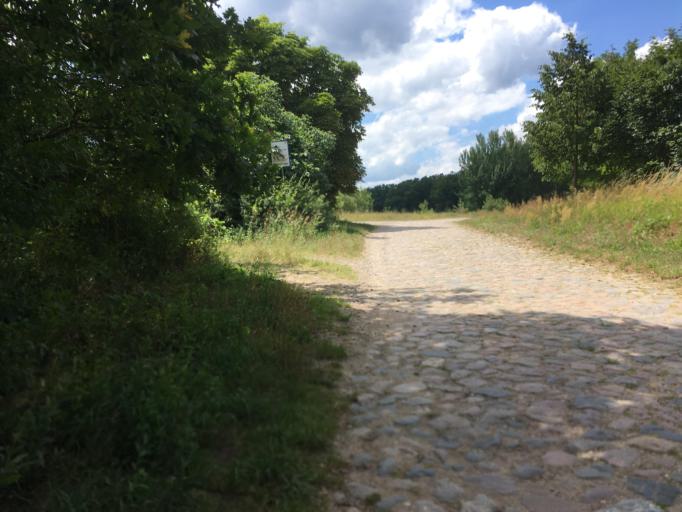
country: DE
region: Brandenburg
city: Althuttendorf
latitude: 52.9575
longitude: 13.7876
